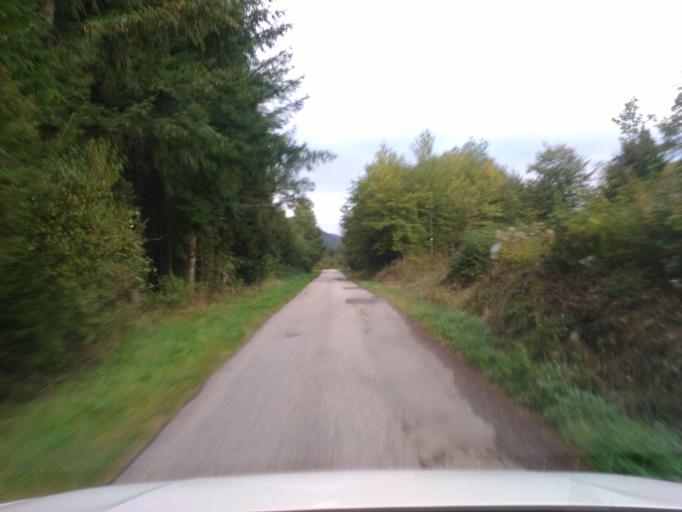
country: FR
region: Lorraine
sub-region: Departement des Vosges
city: Senones
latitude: 48.3946
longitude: 7.0376
